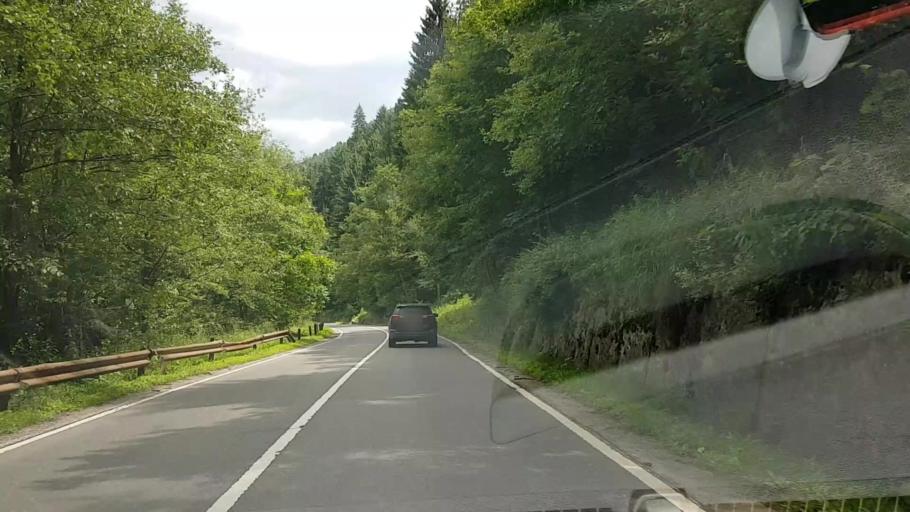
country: RO
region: Neamt
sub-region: Comuna Farcasa
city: Farcasa
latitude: 47.1375
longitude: 25.8630
